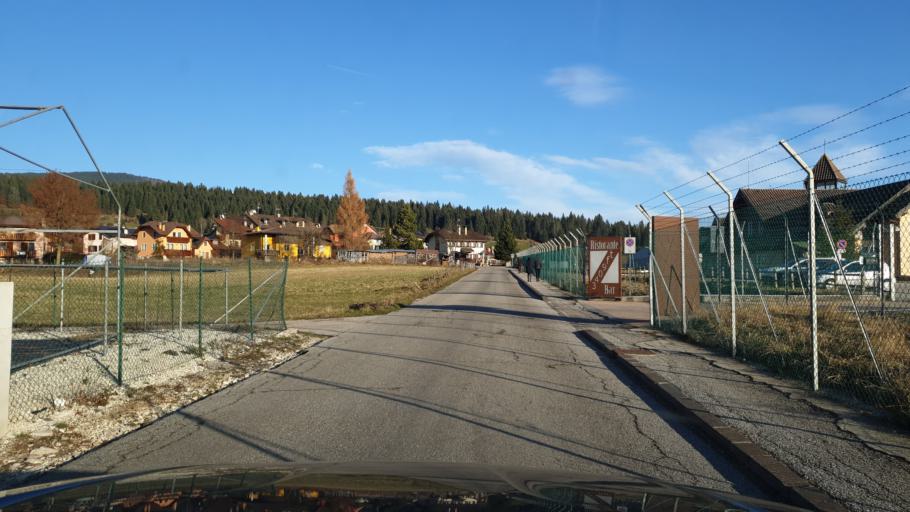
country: IT
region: Veneto
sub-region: Provincia di Vicenza
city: Asiago
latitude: 45.8884
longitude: 11.5184
